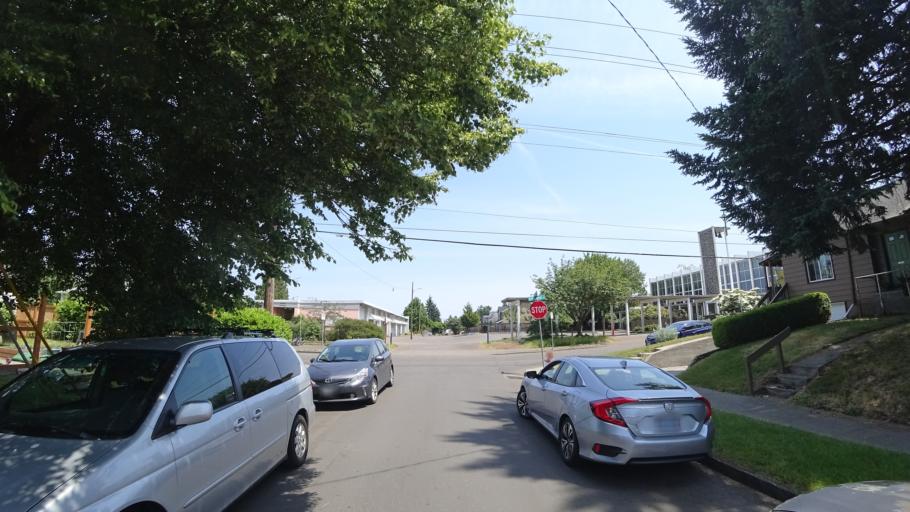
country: US
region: Oregon
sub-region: Multnomah County
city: Portland
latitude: 45.5785
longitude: -122.6927
